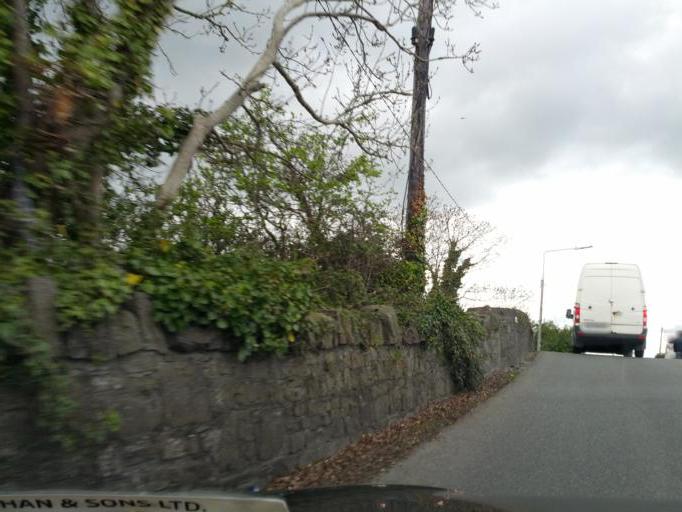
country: IE
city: Confey
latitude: 53.3738
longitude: -6.4852
